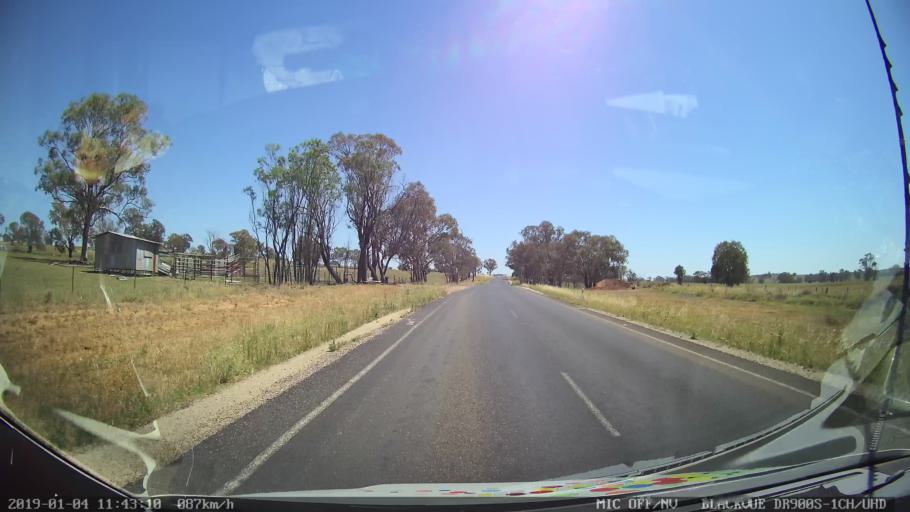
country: AU
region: New South Wales
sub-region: Cabonne
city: Molong
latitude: -32.9724
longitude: 148.7843
